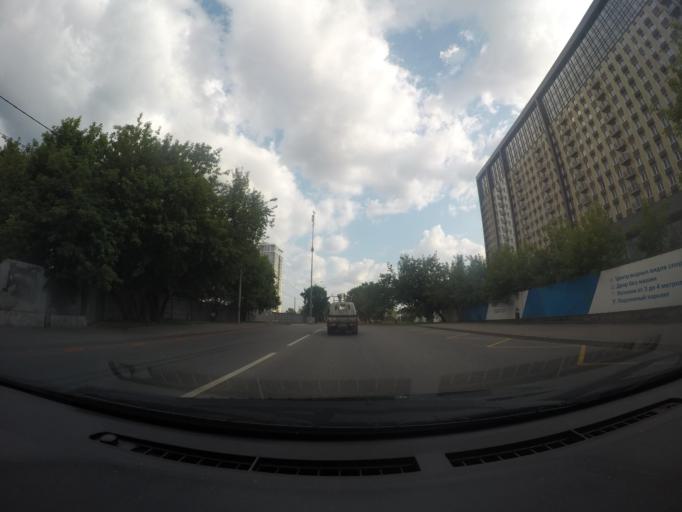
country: RU
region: Moscow
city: Sviblovo
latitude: 55.8502
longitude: 37.6261
